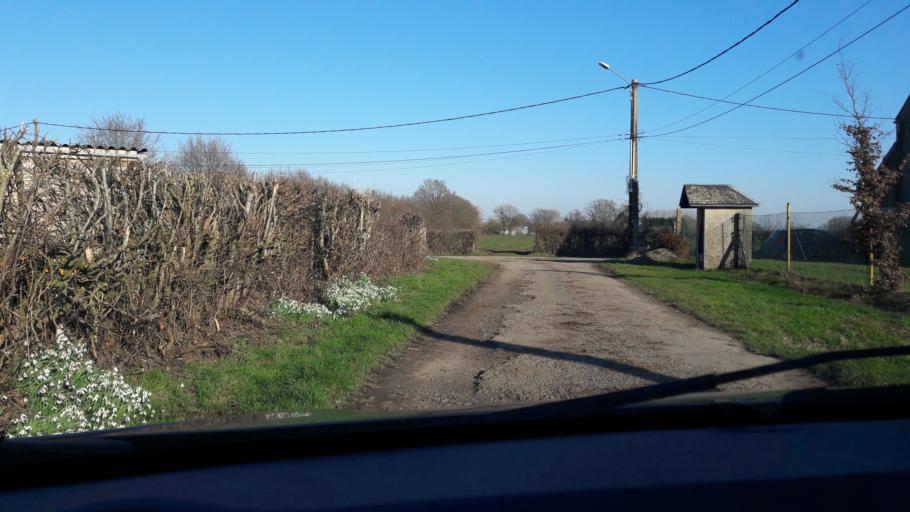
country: BE
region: Wallonia
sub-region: Province du Hainaut
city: Beaumont
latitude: 50.2505
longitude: 4.2055
